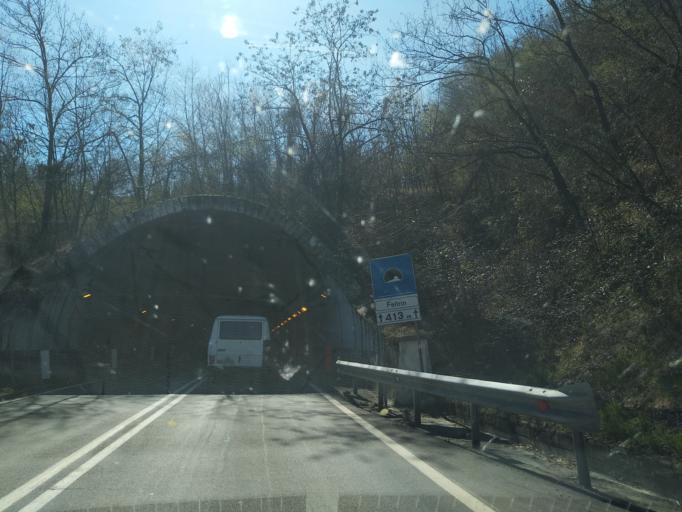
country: IT
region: Emilia-Romagna
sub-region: Provincia di Reggio Emilia
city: Casina
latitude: 44.5155
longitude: 10.4950
